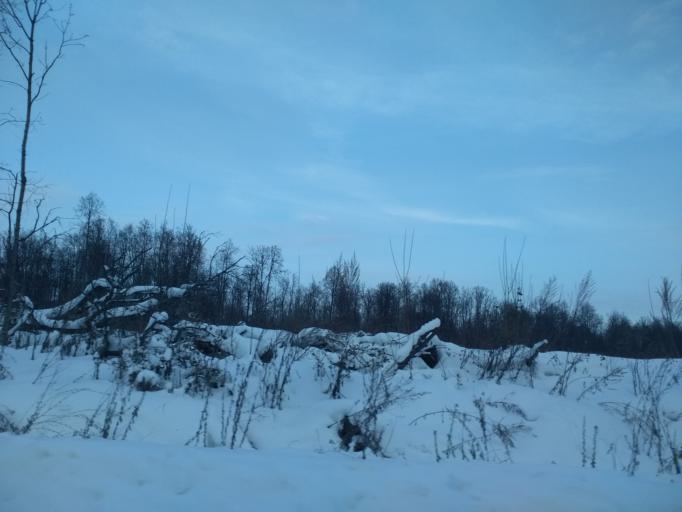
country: RU
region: Bashkortostan
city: Kudeyevskiy
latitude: 54.7128
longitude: 56.6400
